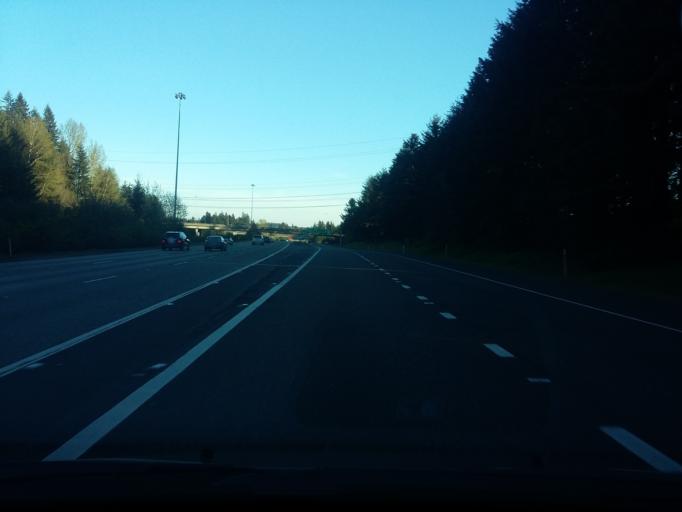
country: US
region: Washington
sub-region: Clark County
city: Orchards
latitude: 45.6627
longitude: -122.5767
